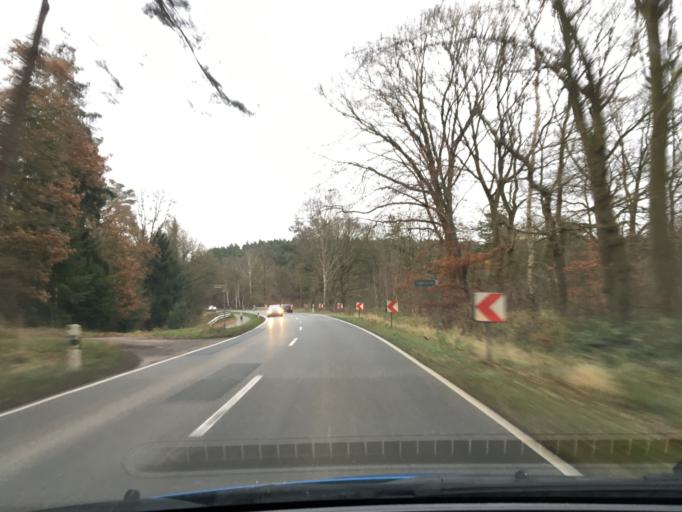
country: DE
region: Lower Saxony
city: Neetze
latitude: 53.2661
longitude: 10.6516
